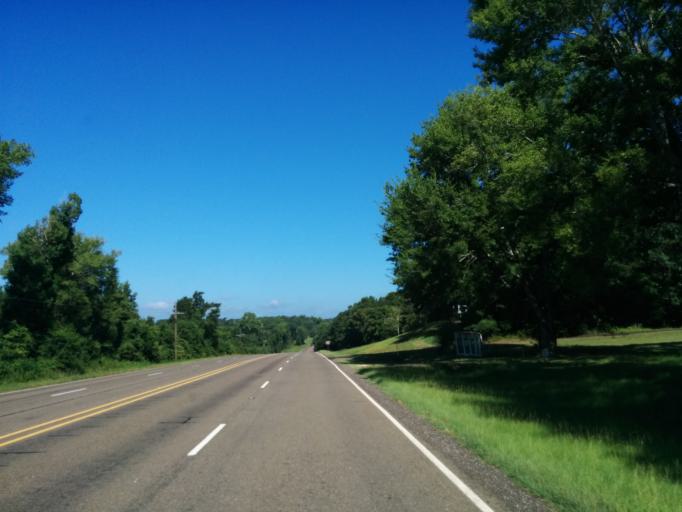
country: US
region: Texas
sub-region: Sabine County
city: Milam
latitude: 31.4318
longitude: -93.8292
